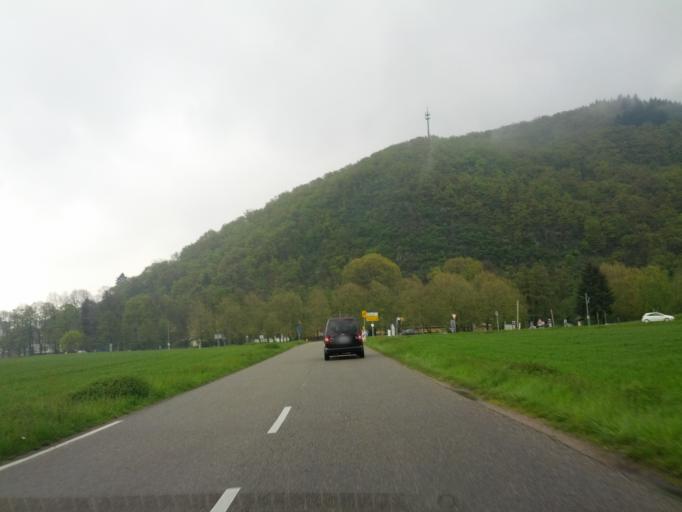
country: DE
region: Baden-Wuerttemberg
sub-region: Freiburg Region
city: Sulzburg
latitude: 47.8713
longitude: 7.7336
